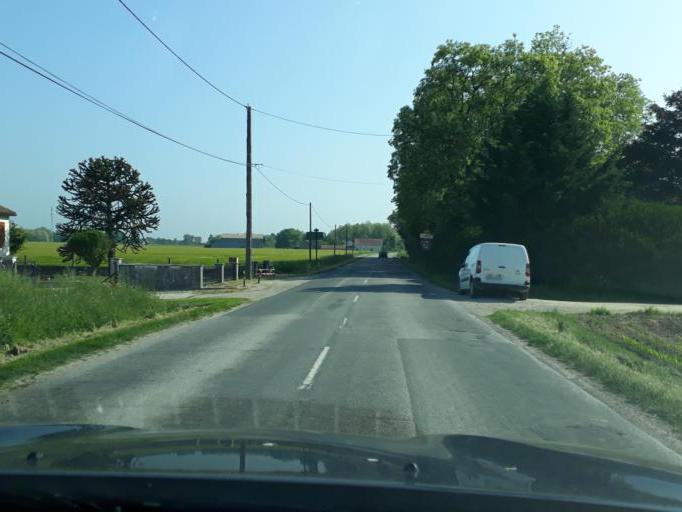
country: FR
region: Centre
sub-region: Departement du Loiret
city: Vennecy
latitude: 47.9359
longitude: 2.0471
